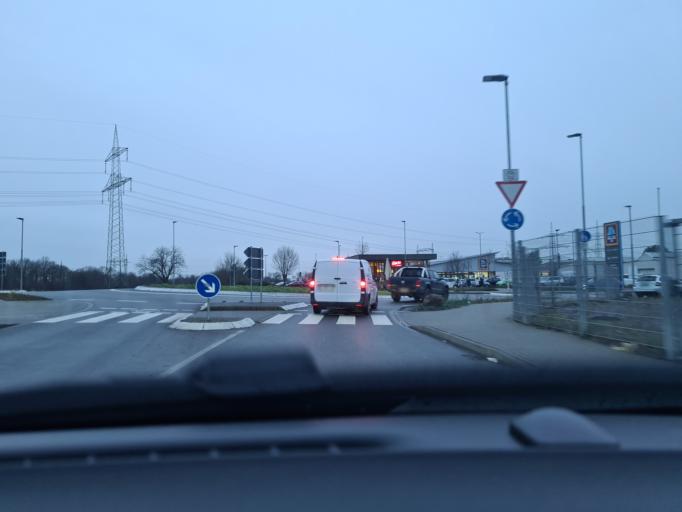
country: DE
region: Baden-Wuerttemberg
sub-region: Karlsruhe Region
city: Wiesloch
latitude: 49.2885
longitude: 8.6793
